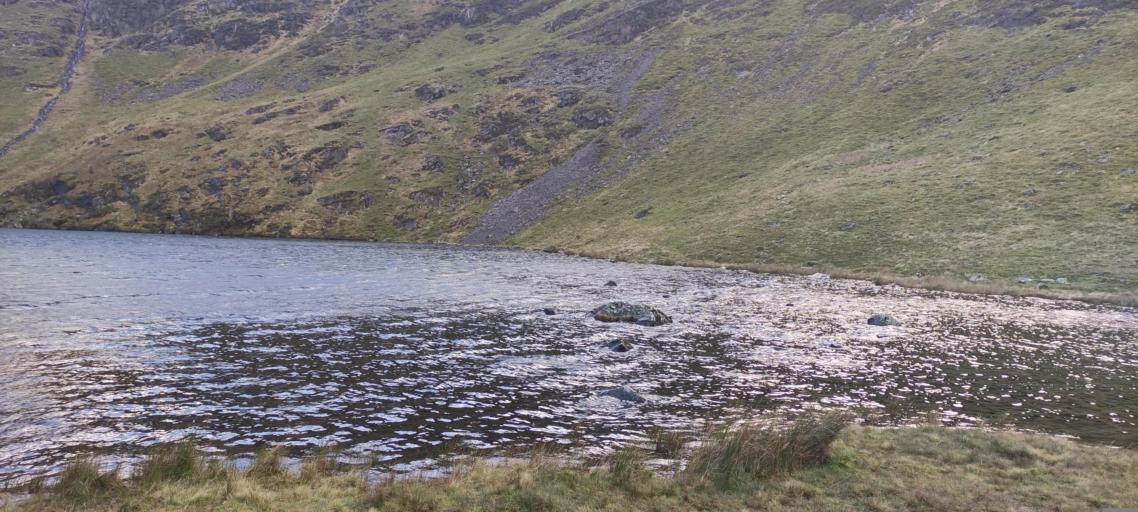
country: GB
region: England
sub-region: Cumbria
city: Keswick
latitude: 54.6738
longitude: -3.0312
